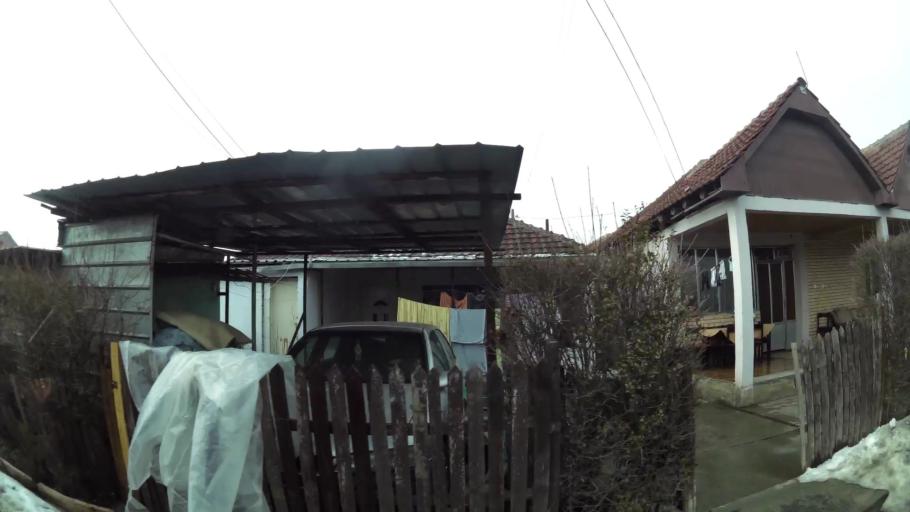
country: MK
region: Ilinden
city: Ilinden
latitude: 41.9922
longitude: 21.5715
